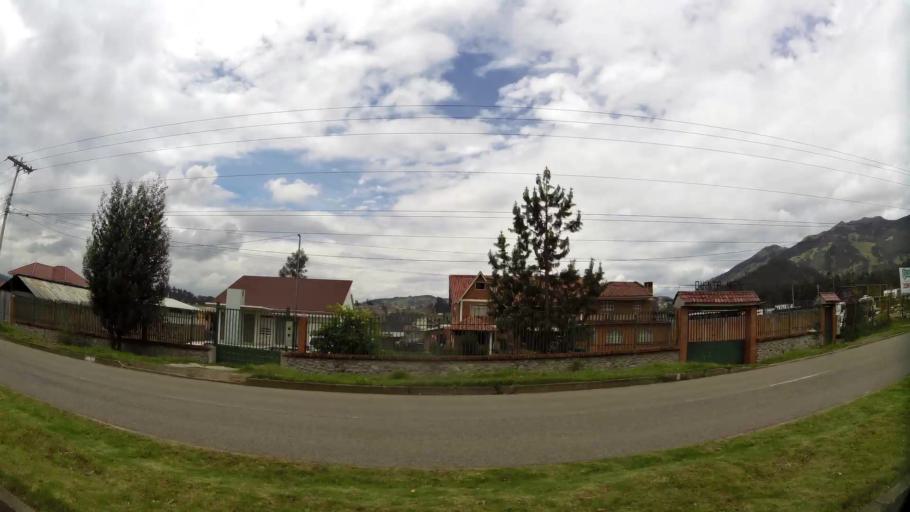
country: EC
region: Azuay
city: Cuenca
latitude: -2.8924
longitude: -79.0556
